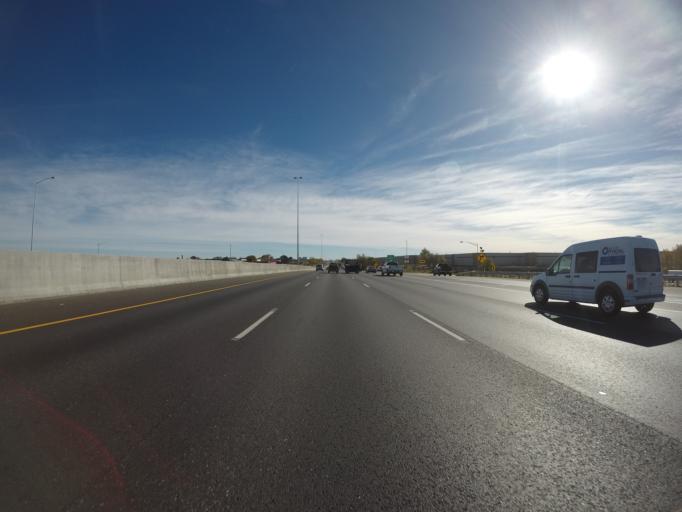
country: US
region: Colorado
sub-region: Adams County
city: Aurora
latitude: 39.7755
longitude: -104.8645
